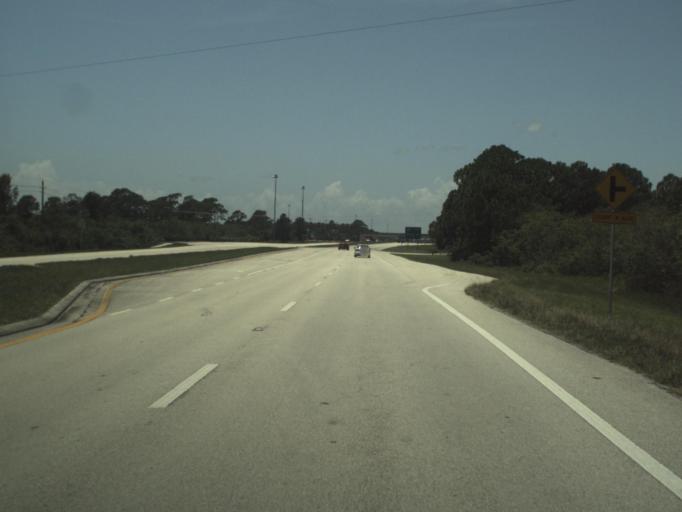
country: US
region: Florida
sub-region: Martin County
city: Palm City
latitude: 27.1620
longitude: -80.3819
